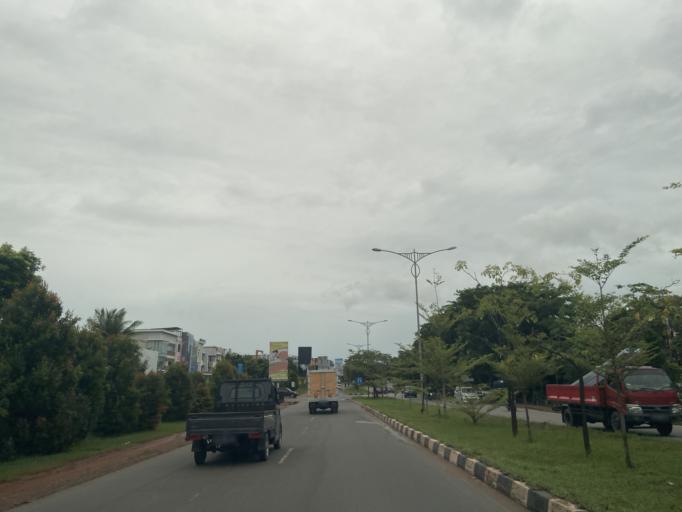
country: SG
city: Singapore
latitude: 1.1188
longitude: 104.0582
